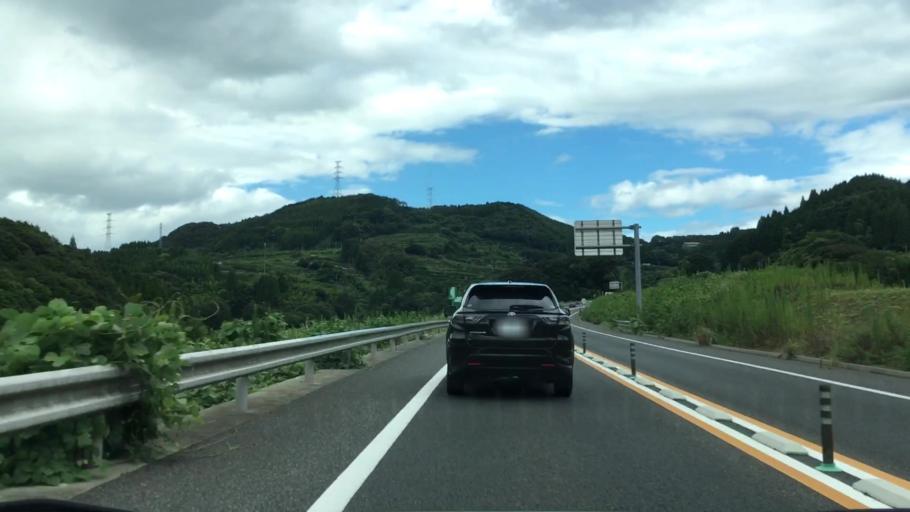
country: JP
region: Saga Prefecture
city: Karatsu
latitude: 33.3918
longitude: 129.9347
